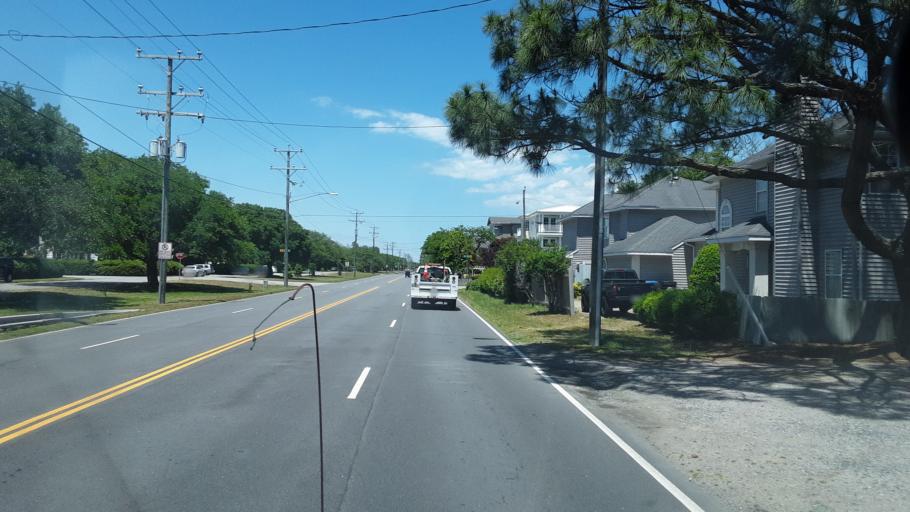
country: US
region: Virginia
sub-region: City of Virginia Beach
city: Virginia Beach
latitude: 36.8969
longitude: -75.9902
